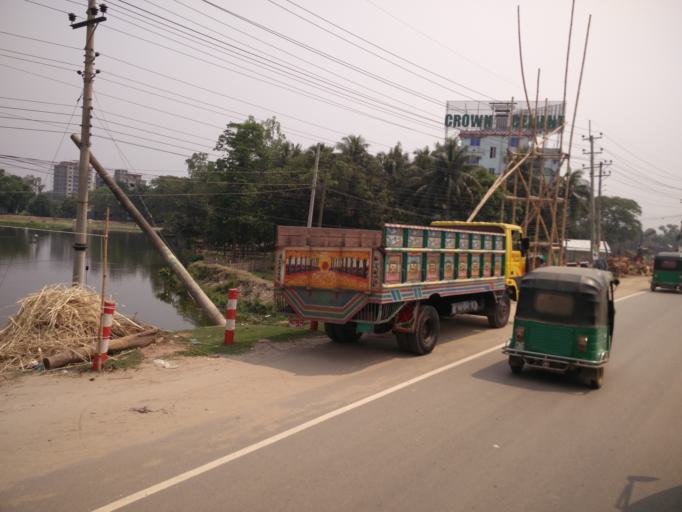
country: BD
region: Dhaka
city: Gafargaon
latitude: 24.4016
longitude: 90.3864
